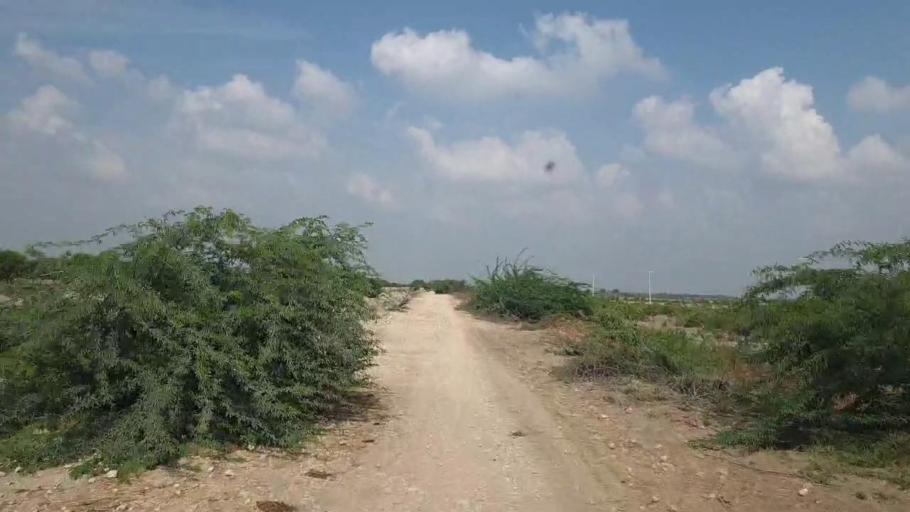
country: PK
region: Sindh
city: Badin
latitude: 24.4985
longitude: 68.6558
